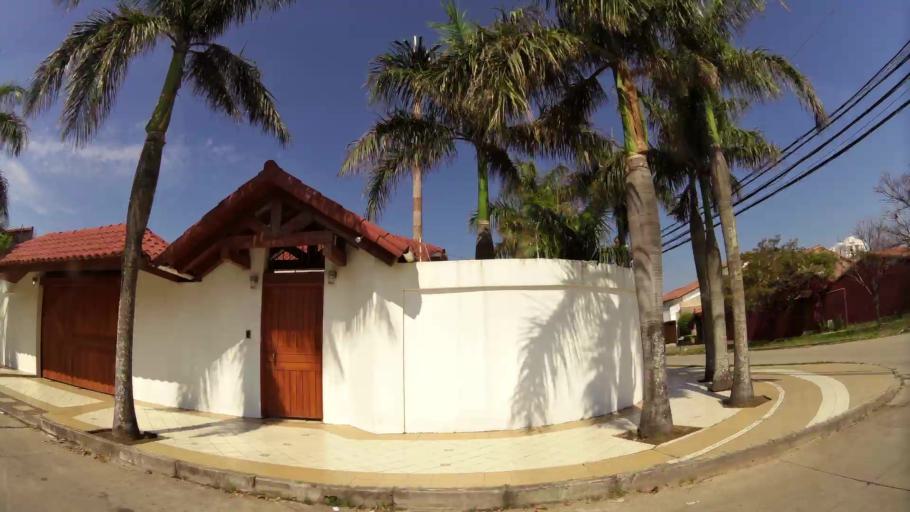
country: BO
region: Santa Cruz
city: Santa Cruz de la Sierra
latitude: -17.7472
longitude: -63.1649
